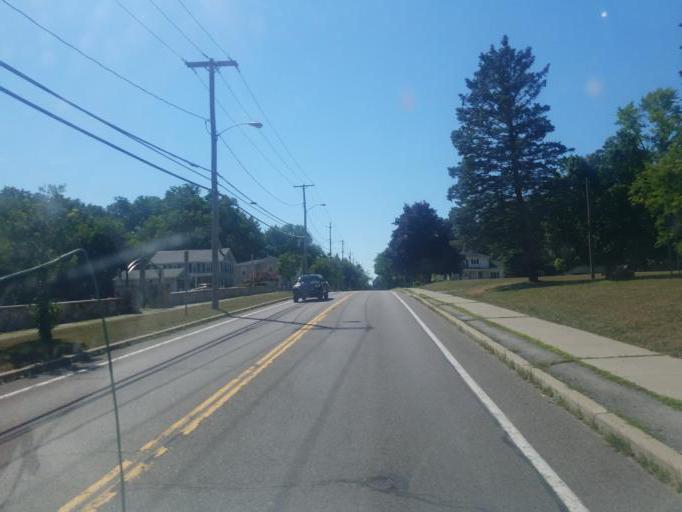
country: US
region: New York
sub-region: Ontario County
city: Phelps
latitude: 42.9593
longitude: -77.0630
